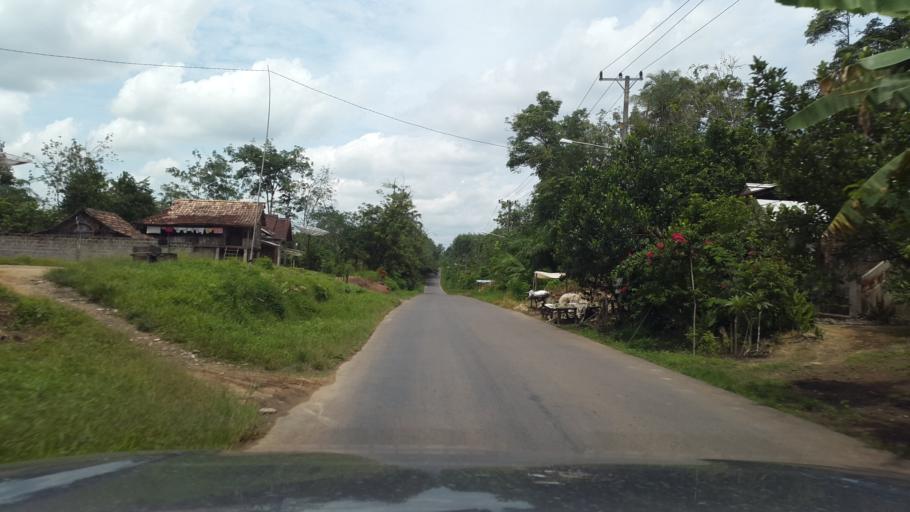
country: ID
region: South Sumatra
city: Gunungmegang Dalam
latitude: -3.3615
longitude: 103.9350
